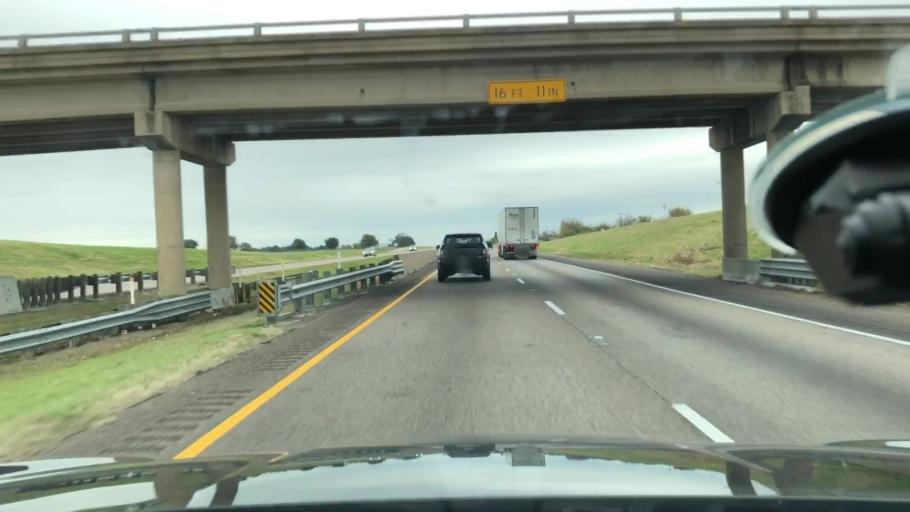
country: US
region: Texas
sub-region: Hopkins County
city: Sulphur Springs
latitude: 33.1475
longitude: -95.5255
